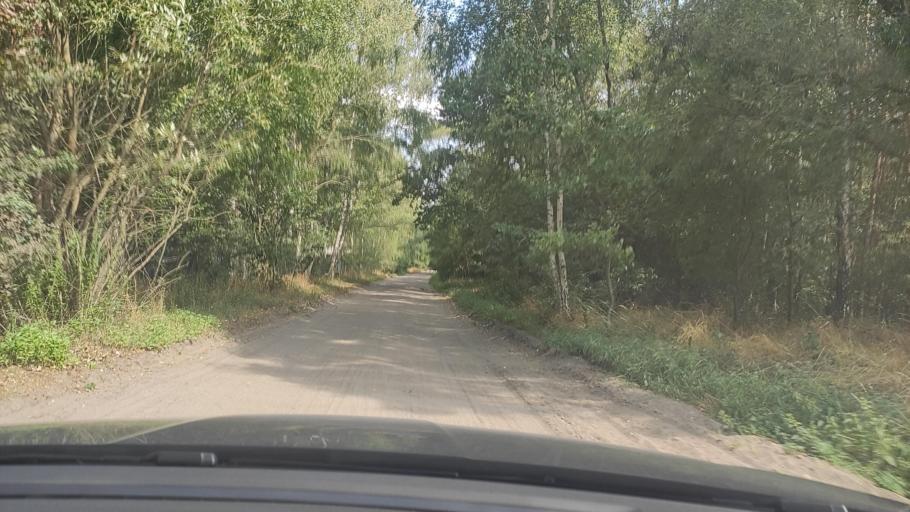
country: PL
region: Greater Poland Voivodeship
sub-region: Powiat poznanski
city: Pobiedziska
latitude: 52.4926
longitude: 17.1994
